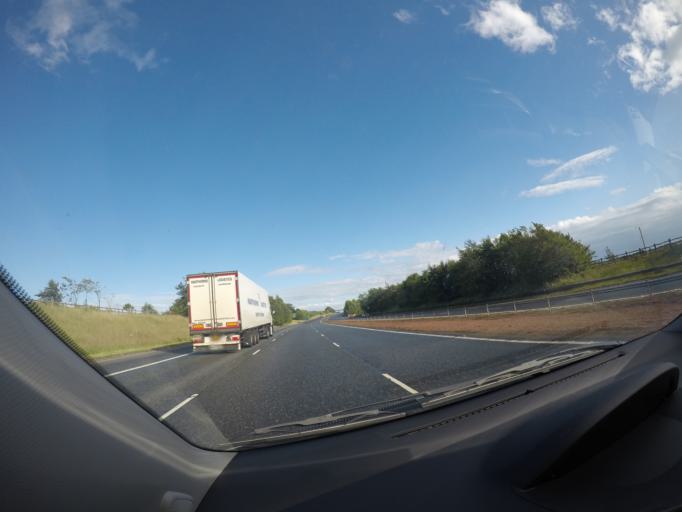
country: GB
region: Scotland
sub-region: Dumfries and Galloway
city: Annan
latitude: 55.0409
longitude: -3.1798
